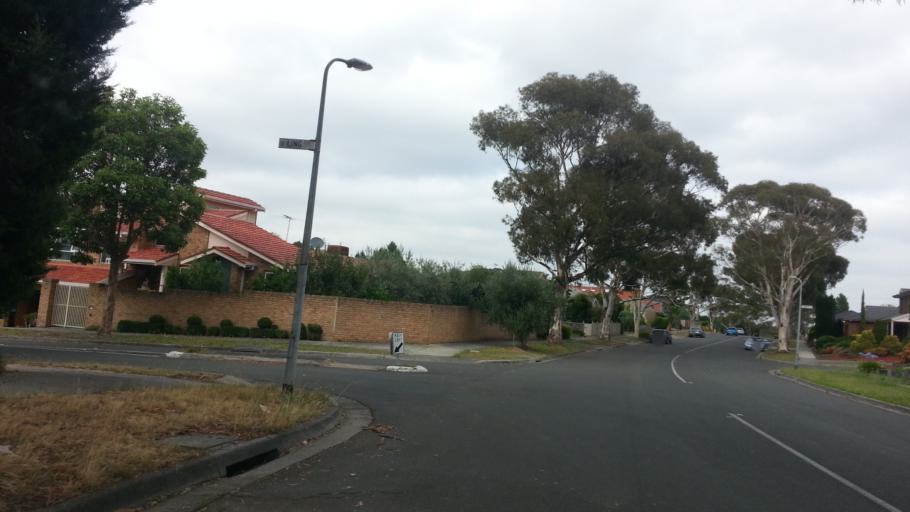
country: AU
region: Victoria
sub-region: Knox
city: Rowville
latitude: -37.9249
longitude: 145.2427
